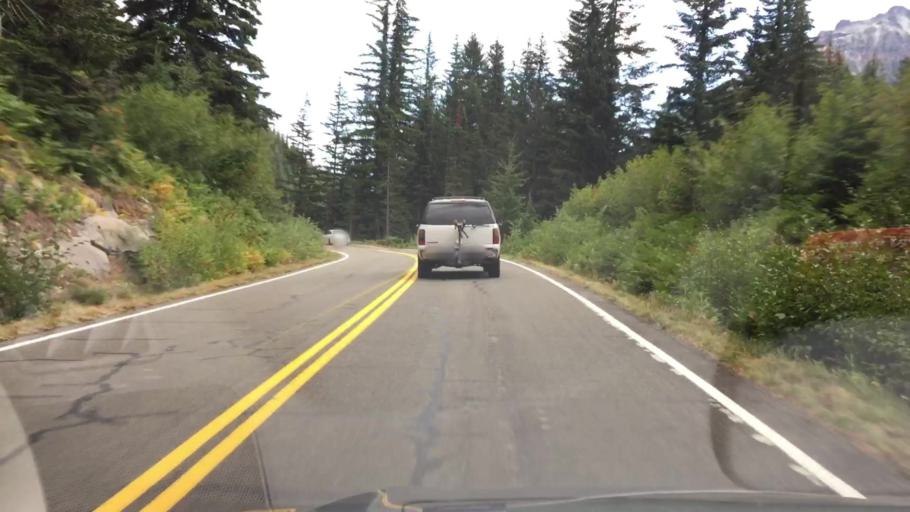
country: US
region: Washington
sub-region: Pierce County
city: Buckley
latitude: 46.7755
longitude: -121.7007
